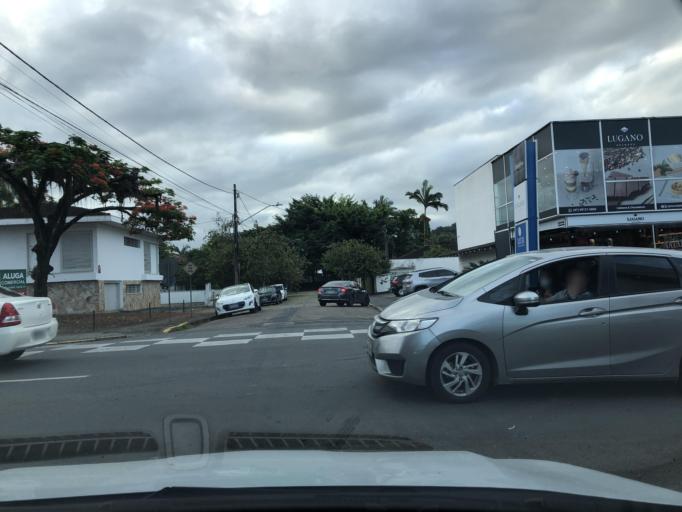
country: BR
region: Santa Catarina
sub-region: Joinville
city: Joinville
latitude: -26.2929
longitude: -48.8500
